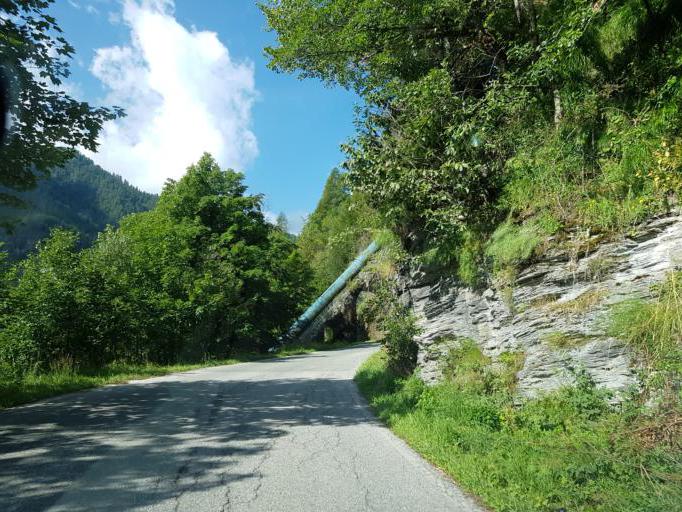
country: IT
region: Piedmont
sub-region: Provincia di Cuneo
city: Casteldelfino
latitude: 44.5885
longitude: 7.0642
